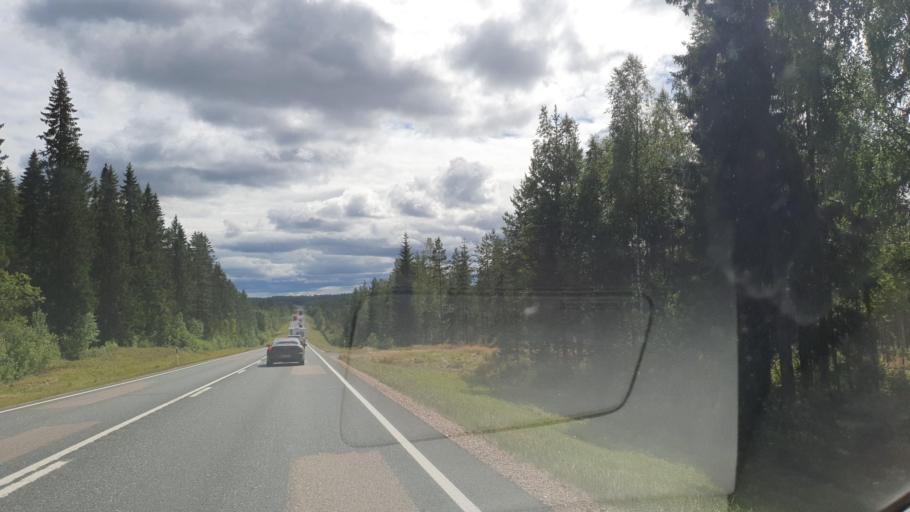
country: FI
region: Kainuu
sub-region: Kajaani
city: Kajaani
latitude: 64.0893
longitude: 27.4532
